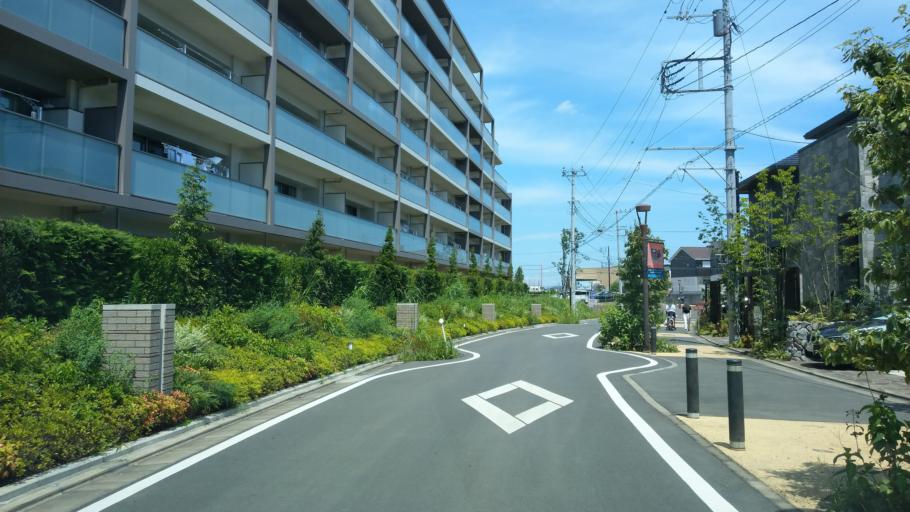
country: JP
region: Saitama
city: Ageoshimo
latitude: 35.9293
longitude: 139.5773
